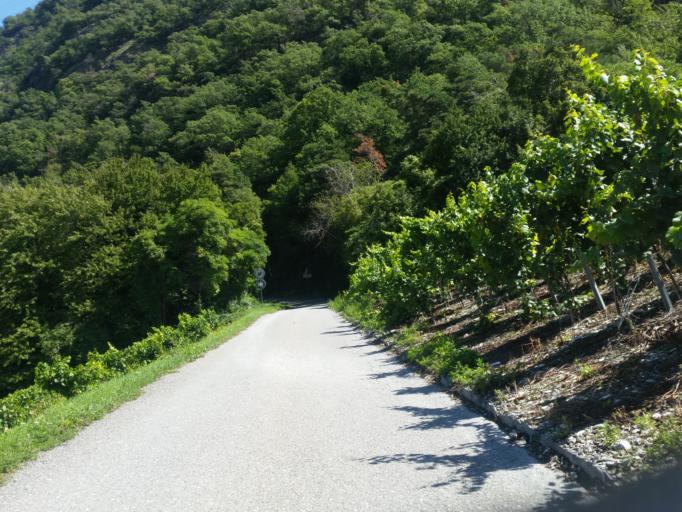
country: CH
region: Valais
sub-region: Martigny District
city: Charrat-les-Chenes
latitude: 46.1227
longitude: 7.1404
